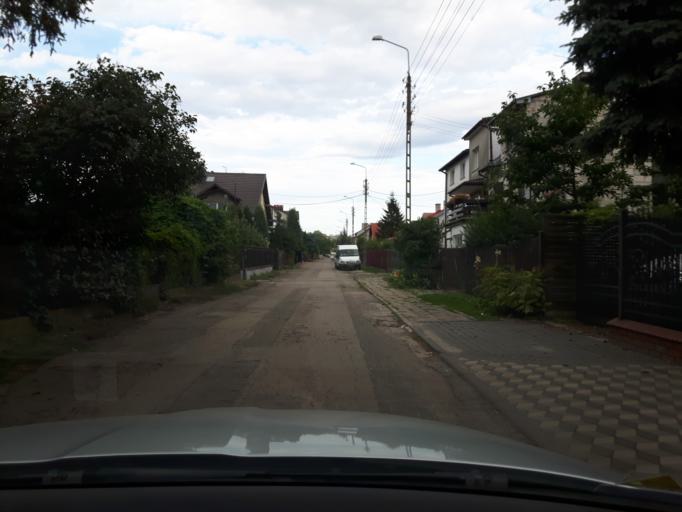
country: PL
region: Masovian Voivodeship
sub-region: Powiat wolominski
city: Zabki
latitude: 52.2917
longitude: 21.1032
